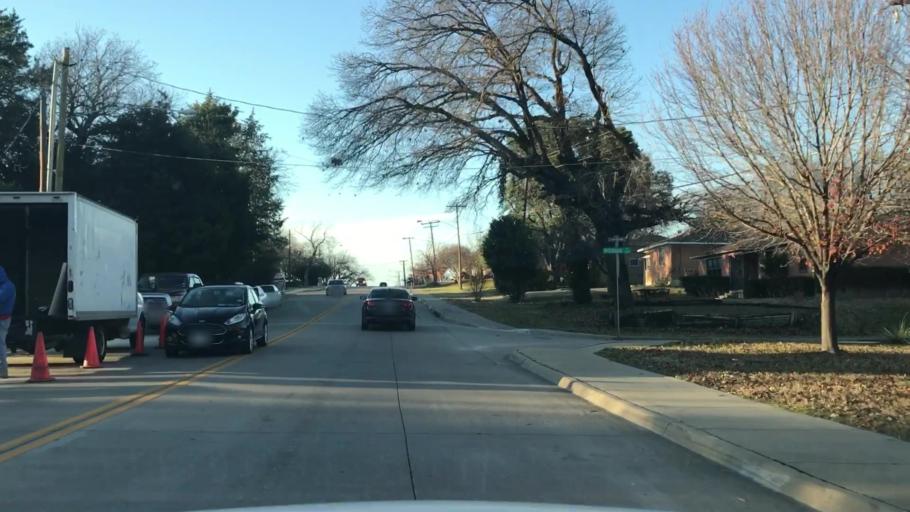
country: US
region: Texas
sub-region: Dallas County
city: Highland Park
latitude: 32.7991
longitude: -96.7108
